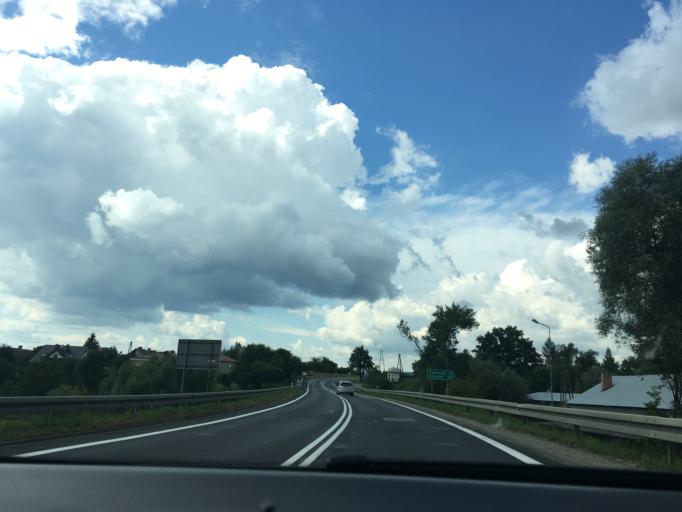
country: PL
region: Subcarpathian Voivodeship
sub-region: Powiat krosnienski
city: Kroscienko Wyzne
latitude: 49.6773
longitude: 21.8511
